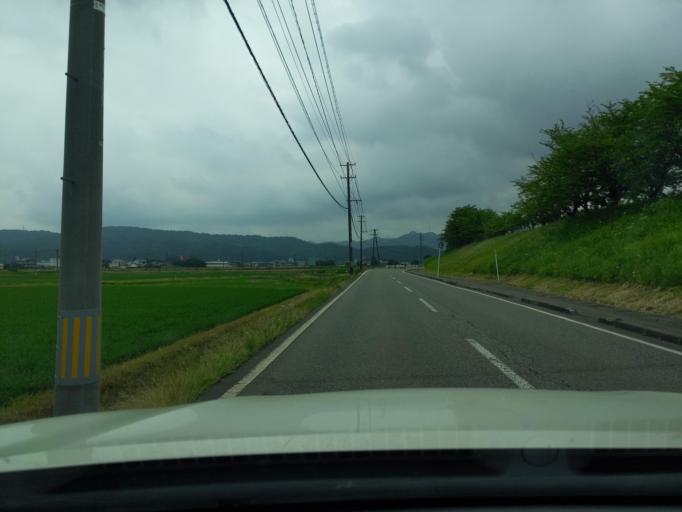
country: JP
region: Niigata
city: Kashiwazaki
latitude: 37.3474
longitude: 138.6015
